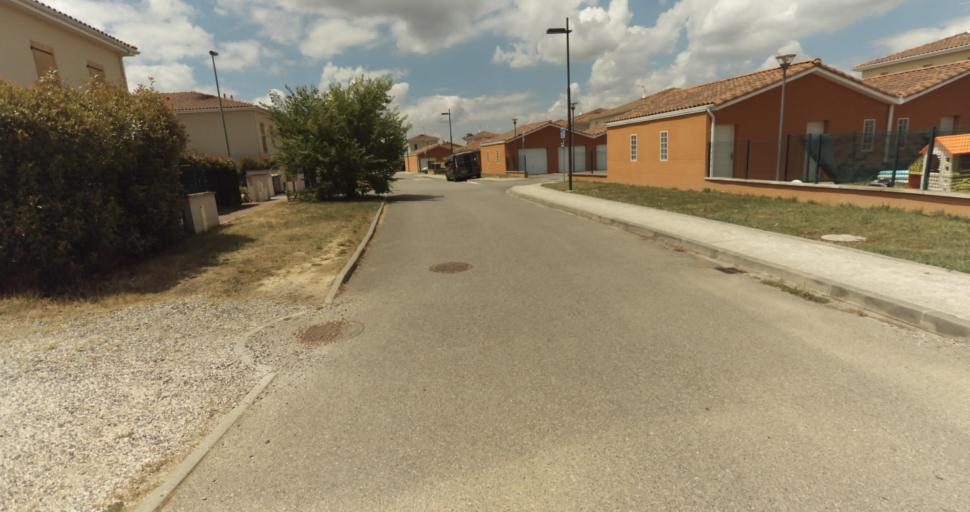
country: FR
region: Midi-Pyrenees
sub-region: Departement de la Haute-Garonne
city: Fontenilles
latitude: 43.5524
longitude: 1.1844
